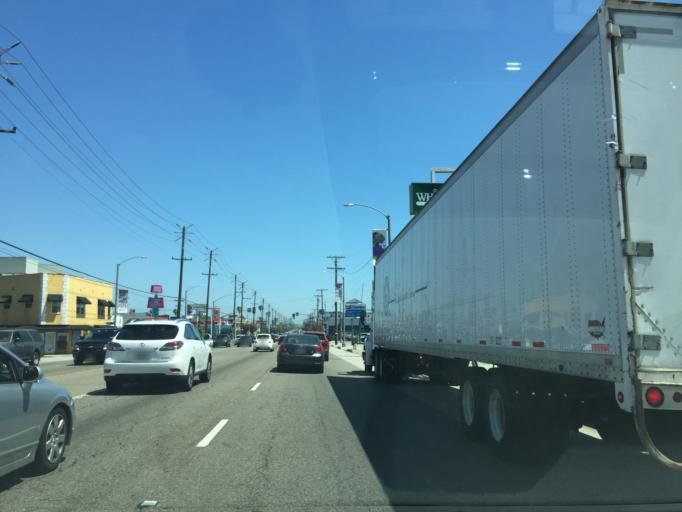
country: US
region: California
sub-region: Los Angeles County
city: Marina del Rey
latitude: 34.0020
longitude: -118.4693
